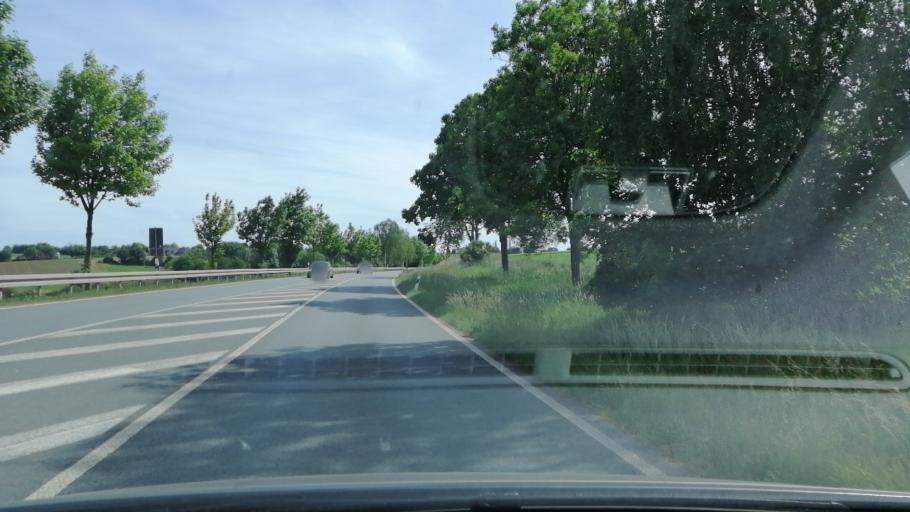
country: DE
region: Hesse
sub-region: Regierungsbezirk Kassel
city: Bad Wildungen
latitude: 51.1419
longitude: 9.1181
